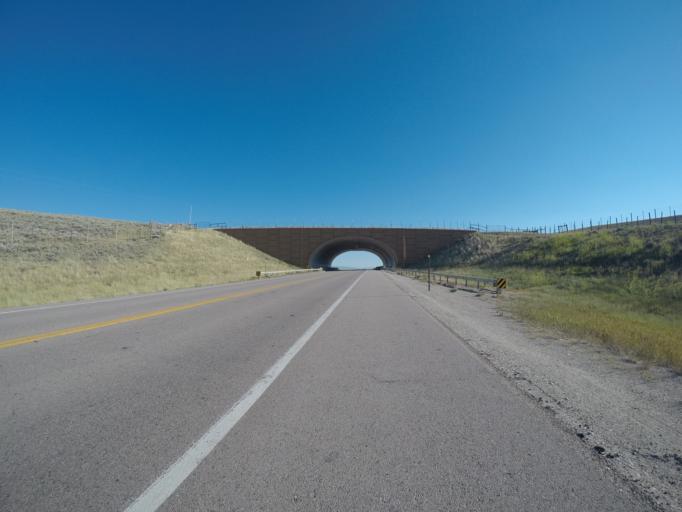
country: US
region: Wyoming
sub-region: Sublette County
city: Pinedale
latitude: 42.9122
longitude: -110.0781
